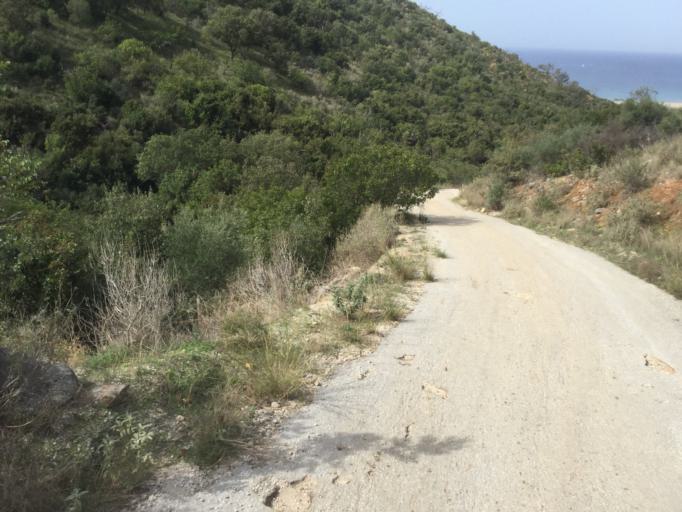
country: GR
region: West Greece
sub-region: Nomos Achaias
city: Lapas
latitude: 38.1736
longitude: 21.3759
